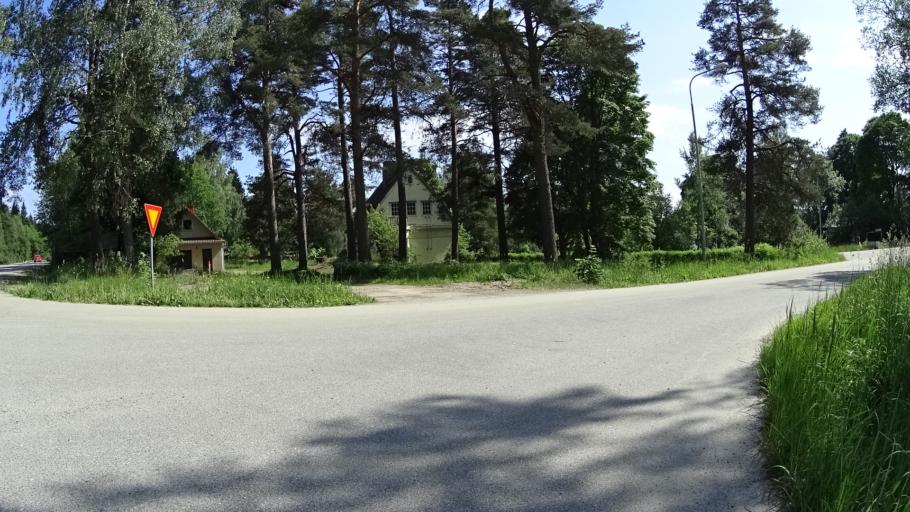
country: FI
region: Uusimaa
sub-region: Raaseporin
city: Karis
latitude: 60.0877
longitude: 23.6499
